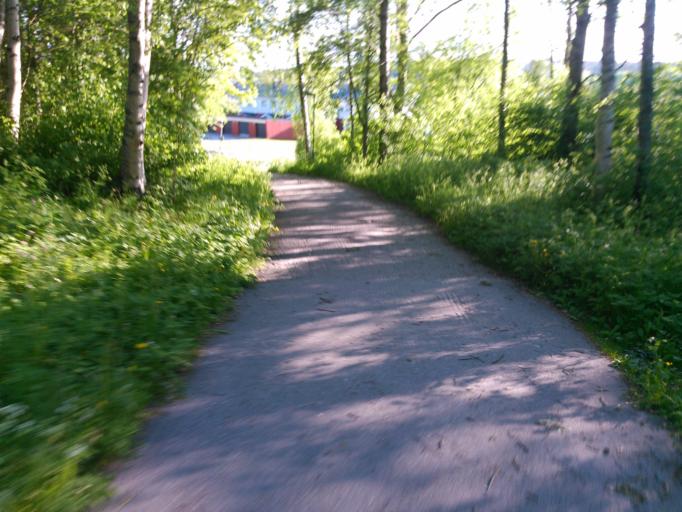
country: SE
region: Vaesterbotten
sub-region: Umea Kommun
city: Ersmark
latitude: 63.8438
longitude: 20.3250
